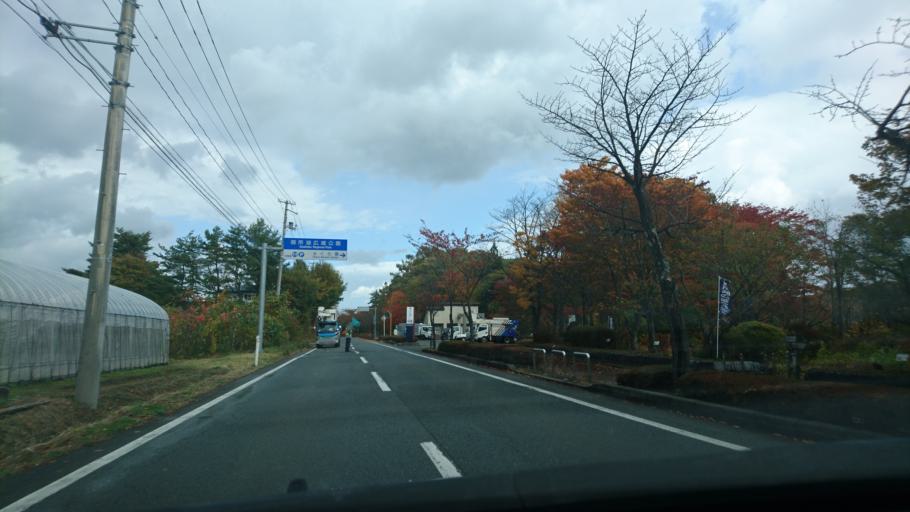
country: JP
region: Iwate
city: Shizukuishi
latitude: 39.6868
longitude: 141.0223
